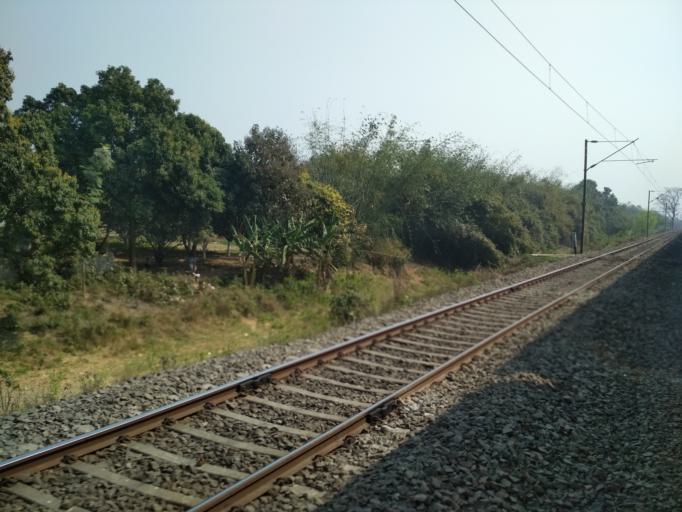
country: IN
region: Bihar
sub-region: Khagaria
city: Khagaria
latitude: 25.5080
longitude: 86.5182
